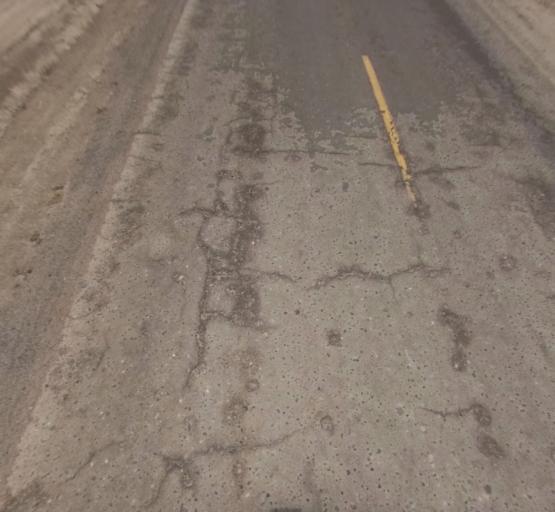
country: US
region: California
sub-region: Fresno County
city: Kerman
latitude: 36.8324
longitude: -120.1872
